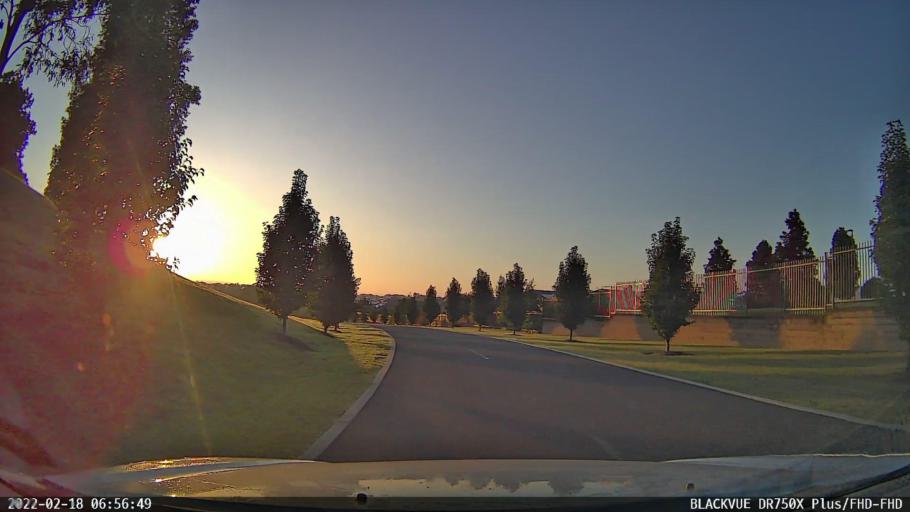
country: AU
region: New South Wales
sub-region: Penrith Municipality
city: Kingswood Park
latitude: -33.7707
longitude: 150.7261
